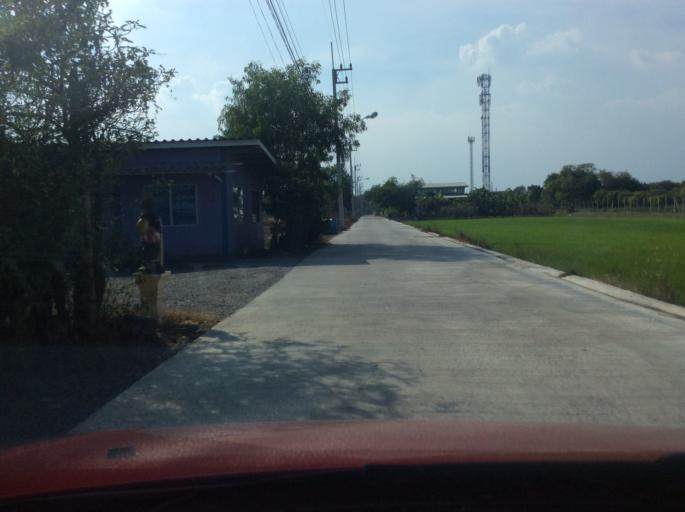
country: TH
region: Pathum Thani
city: Lam Luk Ka
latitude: 13.9677
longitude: 100.7314
